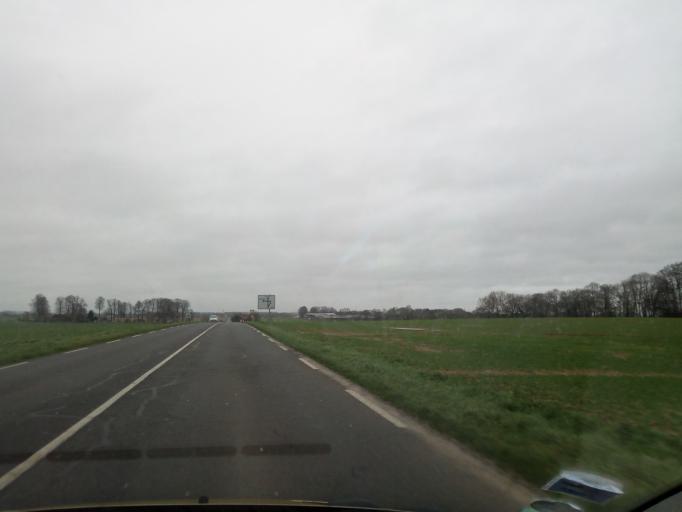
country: FR
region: Haute-Normandie
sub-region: Departement de la Seine-Maritime
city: Auzebosc
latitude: 49.5879
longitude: 0.7332
